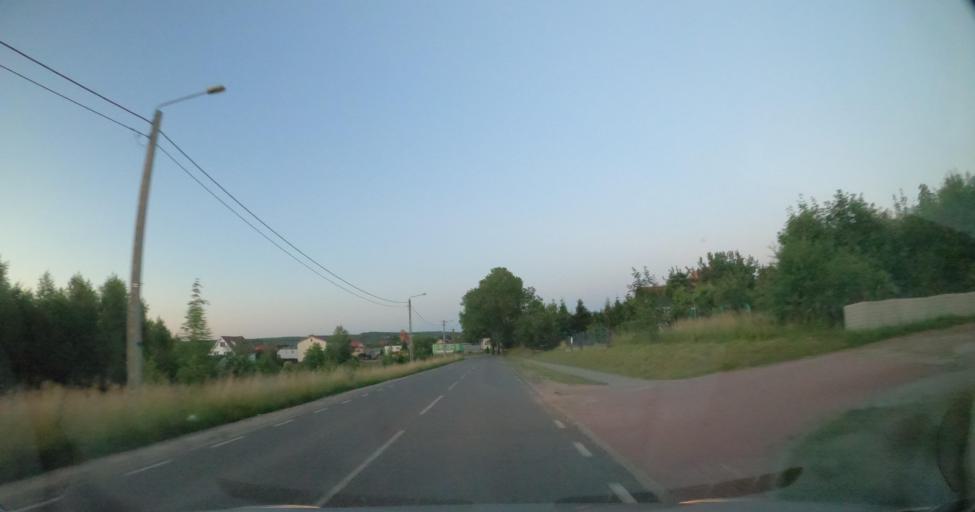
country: PL
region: Pomeranian Voivodeship
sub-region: Powiat wejherowski
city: Szemud
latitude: 54.4845
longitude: 18.2168
